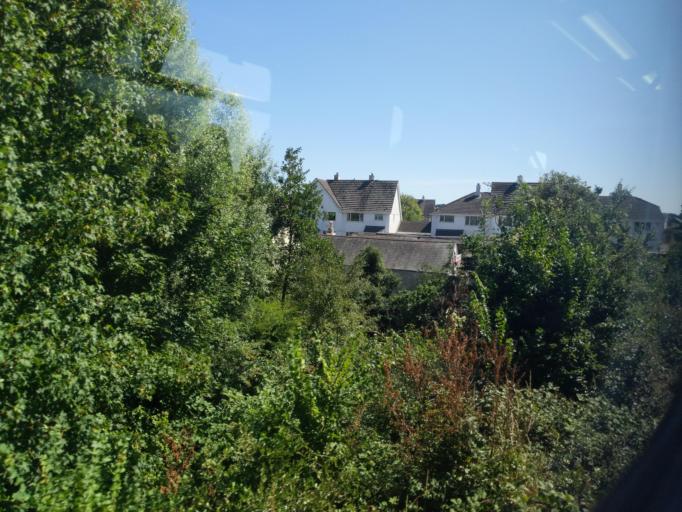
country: GB
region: England
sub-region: Borough of Torbay
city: Paignton
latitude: 50.4408
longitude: -3.5623
